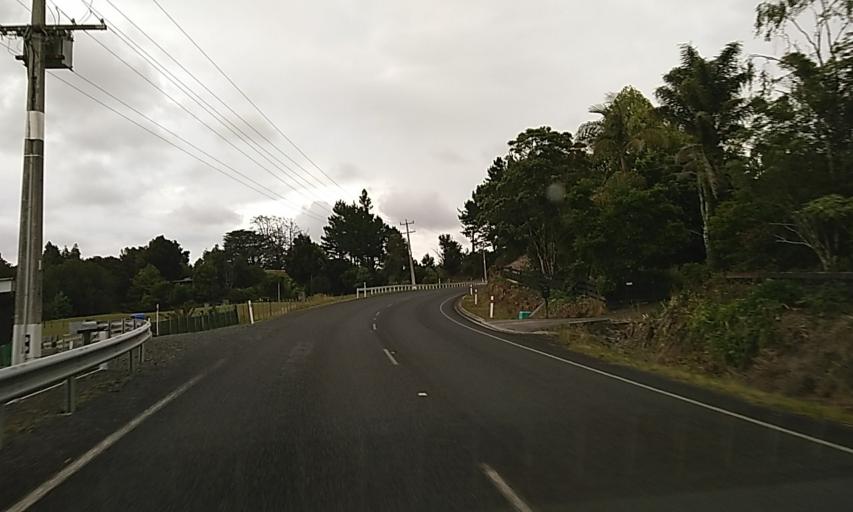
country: NZ
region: Auckland
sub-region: Auckland
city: Pukekohe East
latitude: -37.3121
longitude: 174.9382
